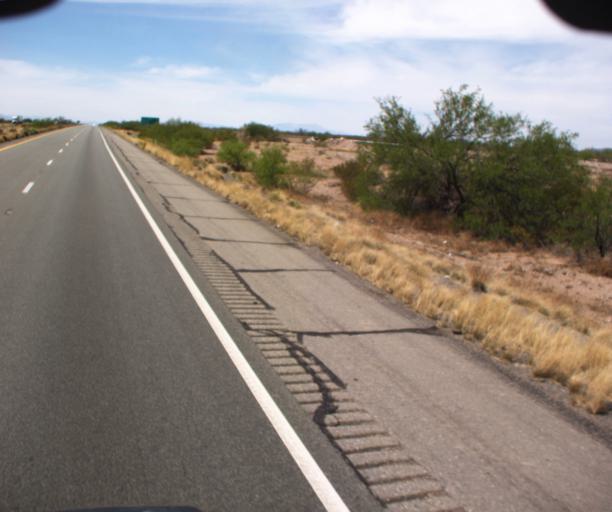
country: US
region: New Mexico
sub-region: Hidalgo County
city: Lordsburg
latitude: 32.2406
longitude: -109.1049
